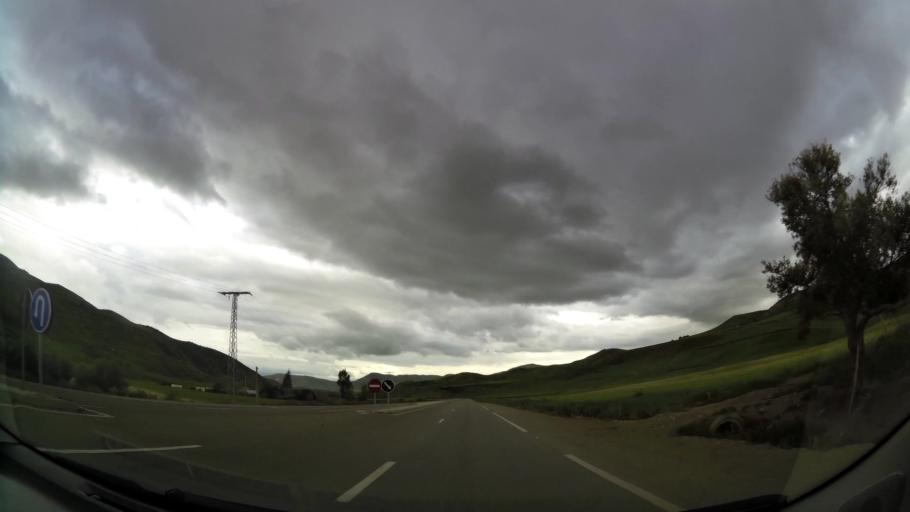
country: MA
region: Taza-Al Hoceima-Taounate
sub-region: Taza
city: Taza
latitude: 34.3379
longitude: -3.9396
